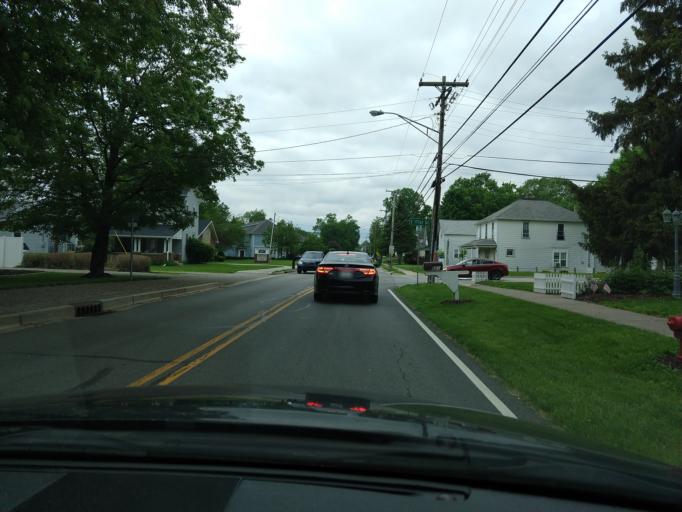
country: US
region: Indiana
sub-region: Hamilton County
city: Westfield
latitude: 40.0363
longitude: -86.1276
